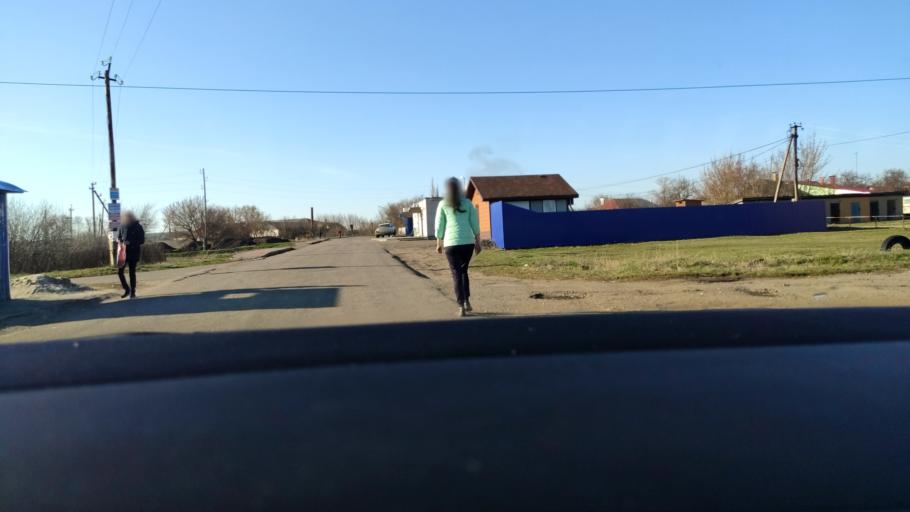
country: RU
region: Voronezj
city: Maslovka
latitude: 51.5019
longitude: 39.2945
